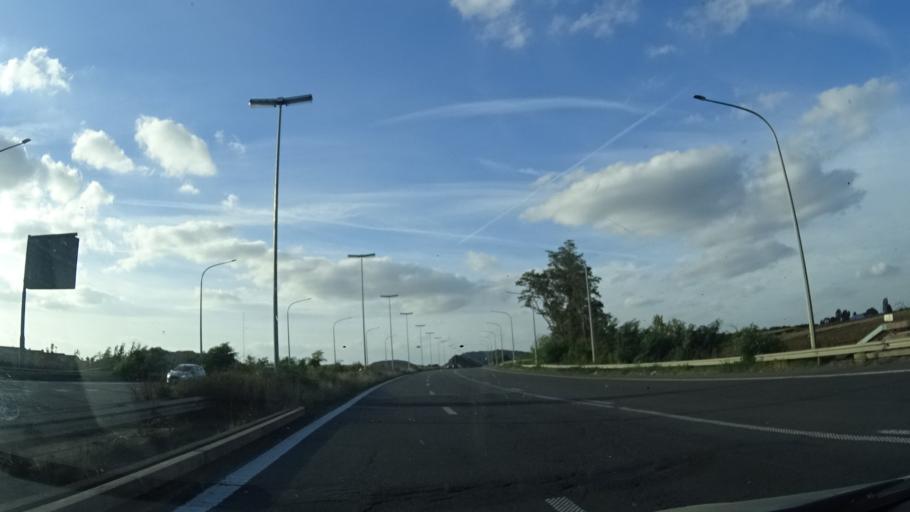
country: BE
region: Wallonia
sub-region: Province du Hainaut
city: Frameries
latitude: 50.4166
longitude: 3.9215
